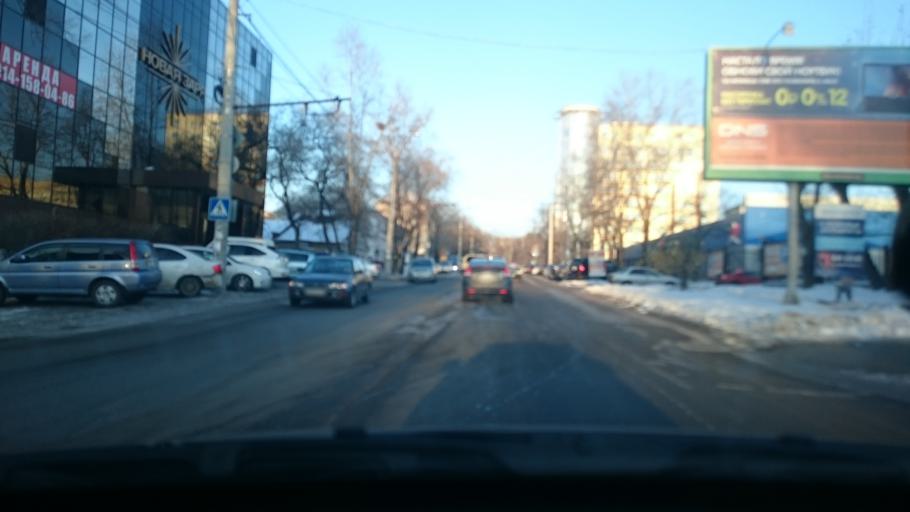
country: RU
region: Khabarovsk Krai
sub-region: Khabarovskiy Rayon
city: Khabarovsk
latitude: 48.4905
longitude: 135.0818
